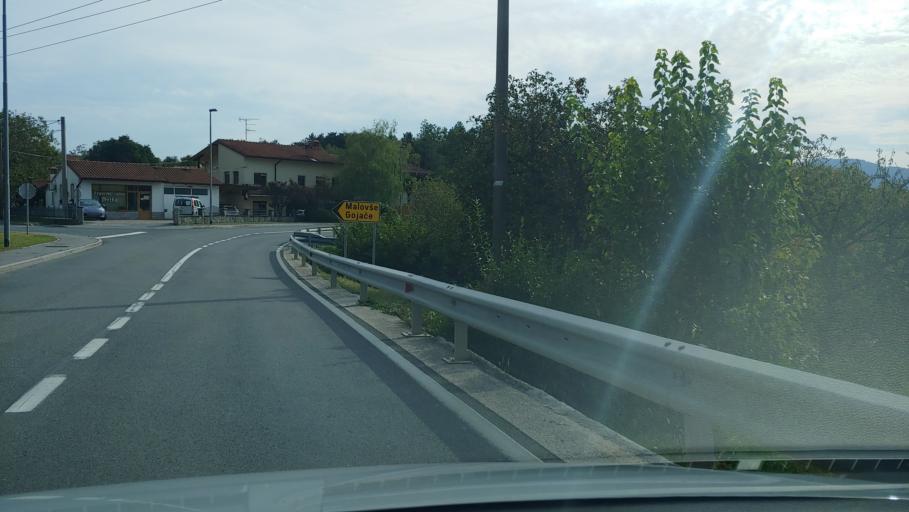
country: SI
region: Nova Gorica
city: Sempas
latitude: 45.9054
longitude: 13.7804
